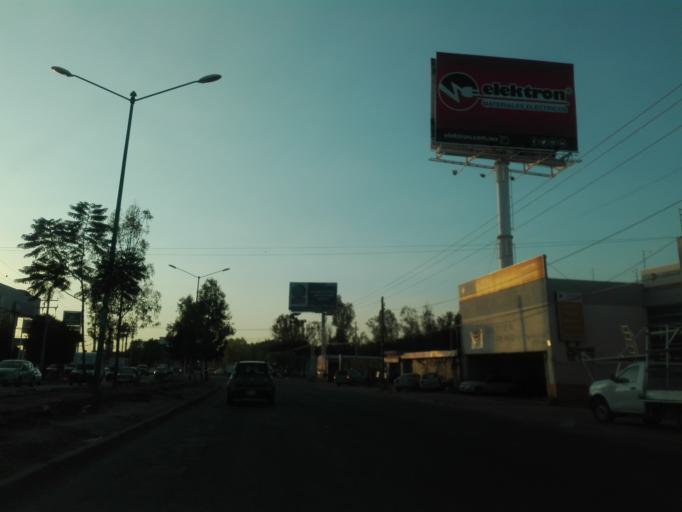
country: MX
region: Guanajuato
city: Leon
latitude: 21.1009
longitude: -101.6742
